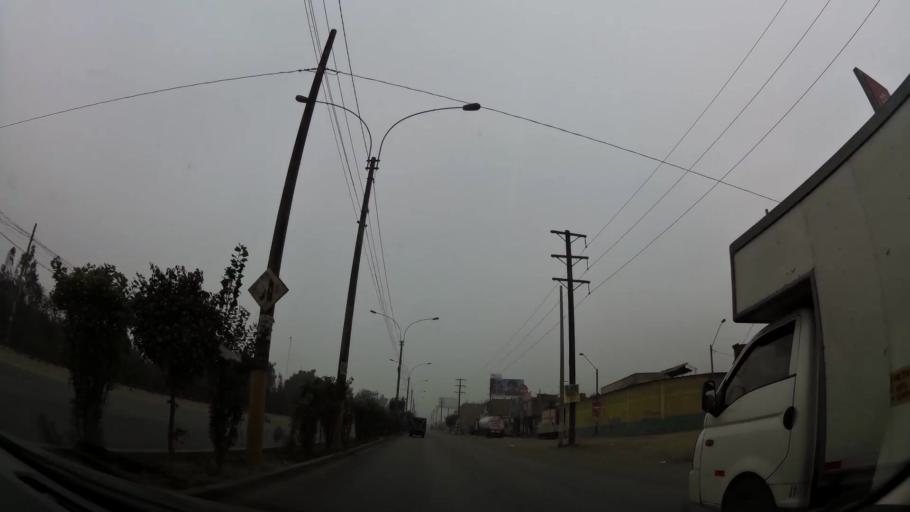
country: PE
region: Lima
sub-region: Lima
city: Santa Maria
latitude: -11.9986
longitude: -76.8371
